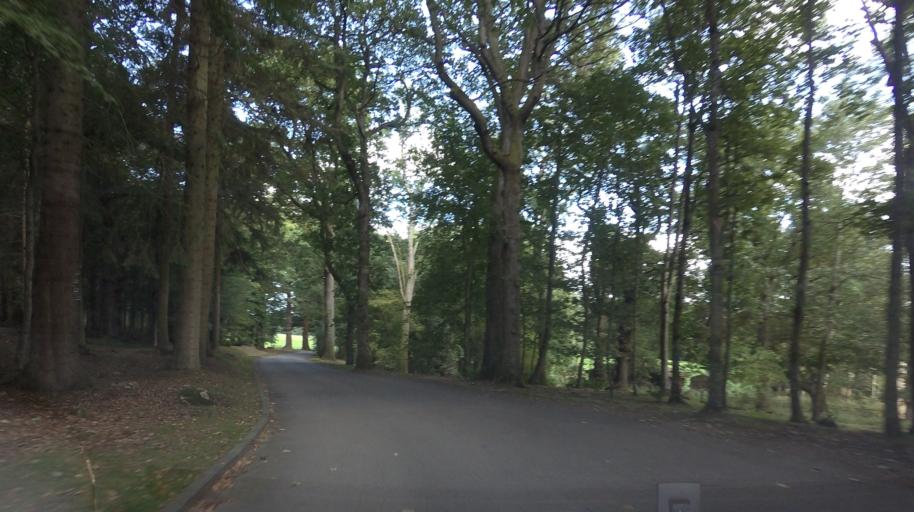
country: GB
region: Scotland
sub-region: Aberdeenshire
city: Banchory
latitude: 57.0599
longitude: -2.4380
